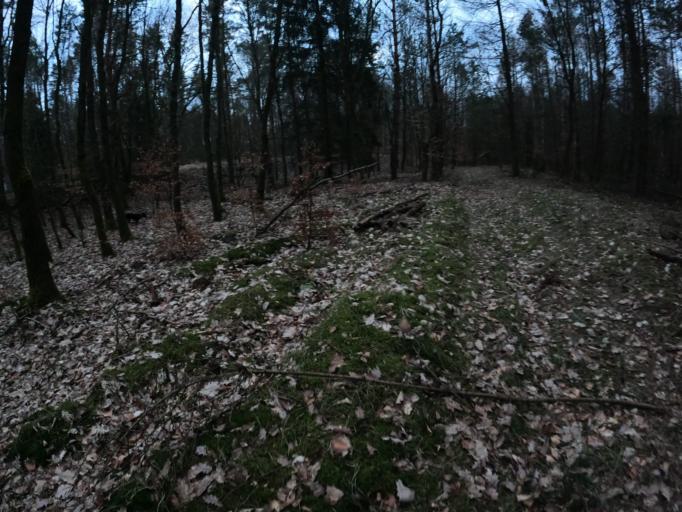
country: PL
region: West Pomeranian Voivodeship
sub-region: Powiat kamienski
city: Golczewo
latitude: 53.8278
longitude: 15.0029
